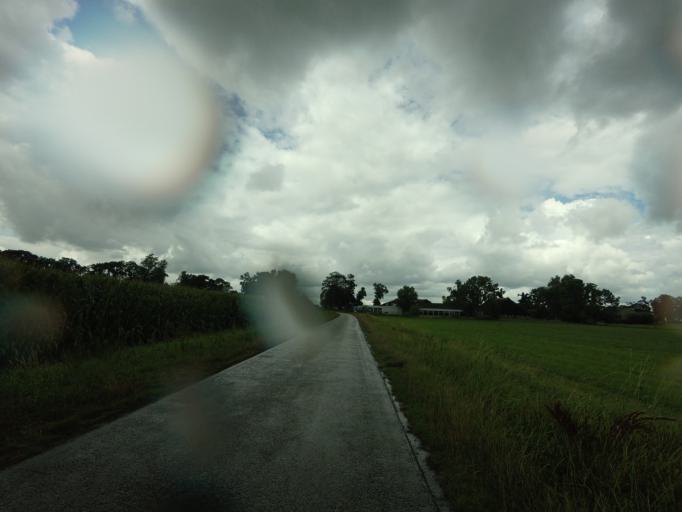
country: NL
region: Overijssel
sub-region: Gemeente Steenwijkerland
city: Wanneperveen
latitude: 52.7218
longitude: 6.1555
